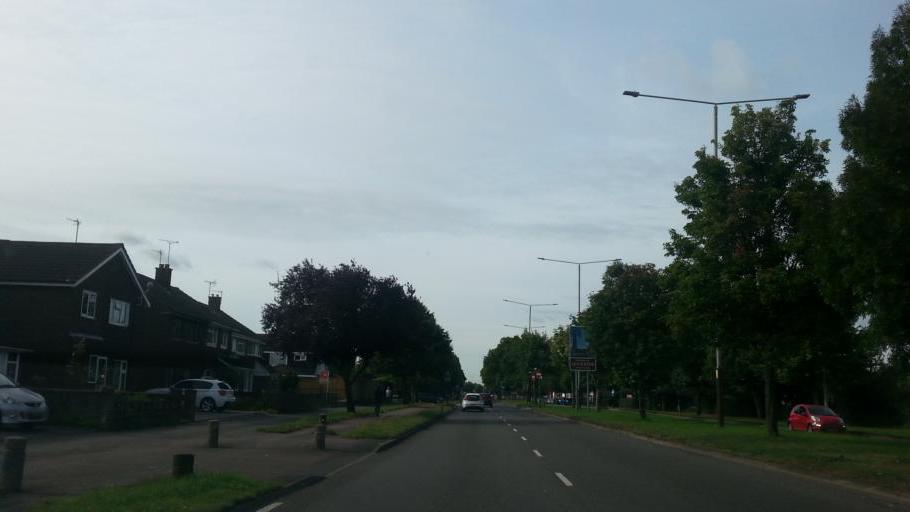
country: GB
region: England
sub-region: Leicestershire
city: Syston
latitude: 52.6719
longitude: -1.1048
